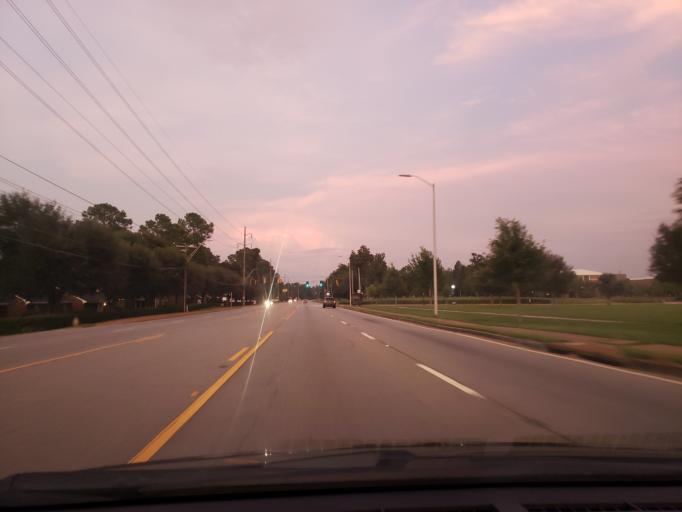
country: US
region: Georgia
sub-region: Dougherty County
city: Albany
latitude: 31.5857
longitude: -84.2155
